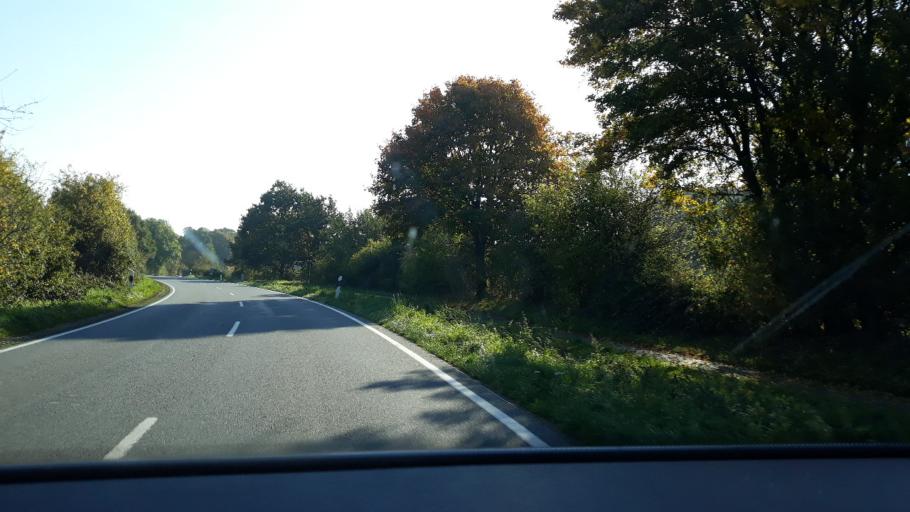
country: DE
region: Schleswig-Holstein
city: Suderfahrenstedt
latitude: 54.5899
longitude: 9.6048
